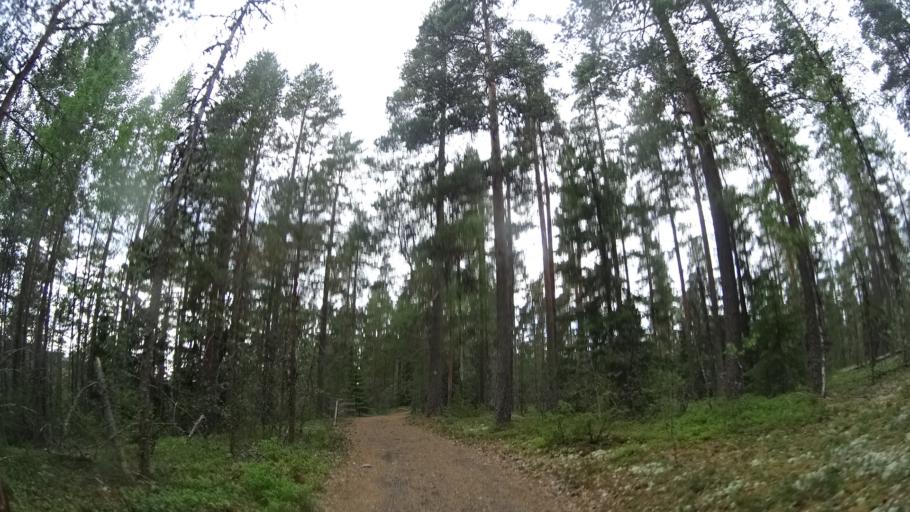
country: FI
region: Satakunta
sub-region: Pohjois-Satakunta
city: Jaemijaervi
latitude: 61.7715
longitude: 22.7383
